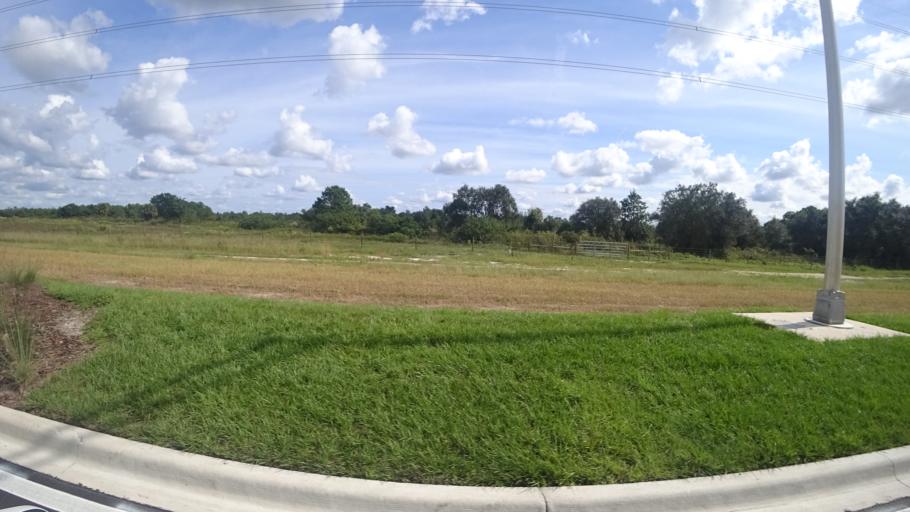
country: US
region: Florida
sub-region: Sarasota County
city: The Meadows
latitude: 27.4086
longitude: -82.3536
